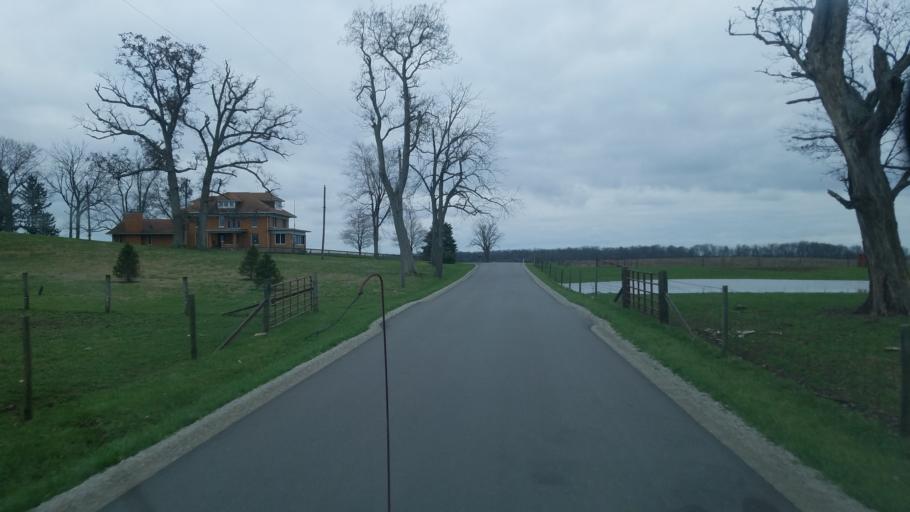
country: US
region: Ohio
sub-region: Fayette County
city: Jeffersonville
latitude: 39.5860
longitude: -83.5167
